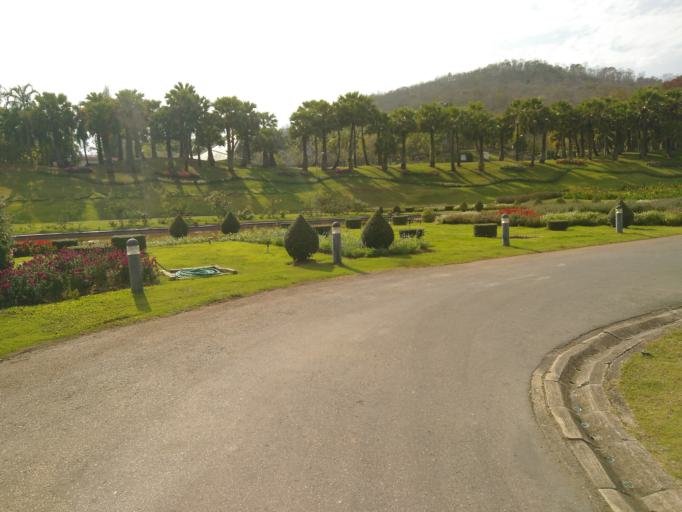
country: TH
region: Chiang Mai
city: Hang Dong
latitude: 18.7524
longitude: 98.9223
